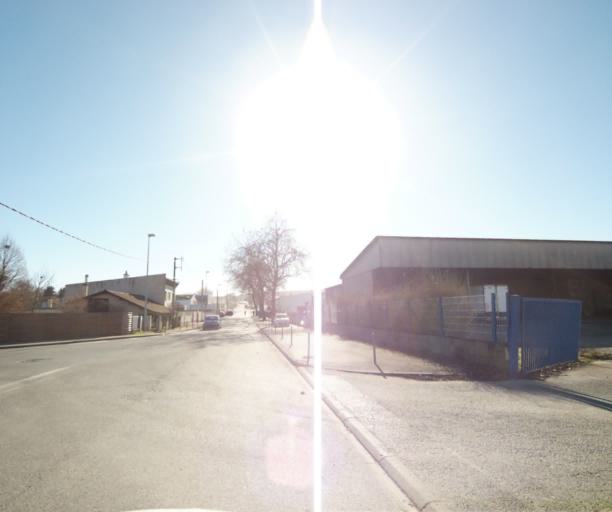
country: FR
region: Lorraine
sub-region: Departement de Meurthe-et-Moselle
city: Vandoeuvre-les-Nancy
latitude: 48.6572
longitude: 6.1876
